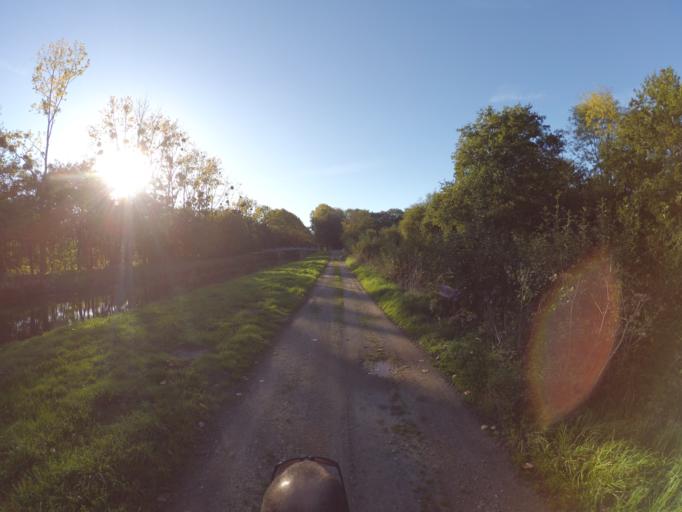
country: FR
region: Brittany
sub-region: Departement du Morbihan
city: Saint-Vincent-sur-Oust
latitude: 47.7205
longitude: -2.1674
